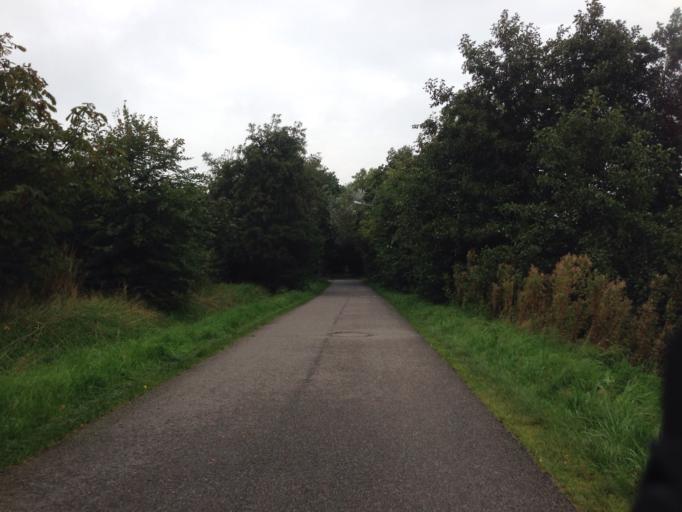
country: DE
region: Schleswig-Holstein
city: Wyk auf Fohr
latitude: 54.6943
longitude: 8.5635
